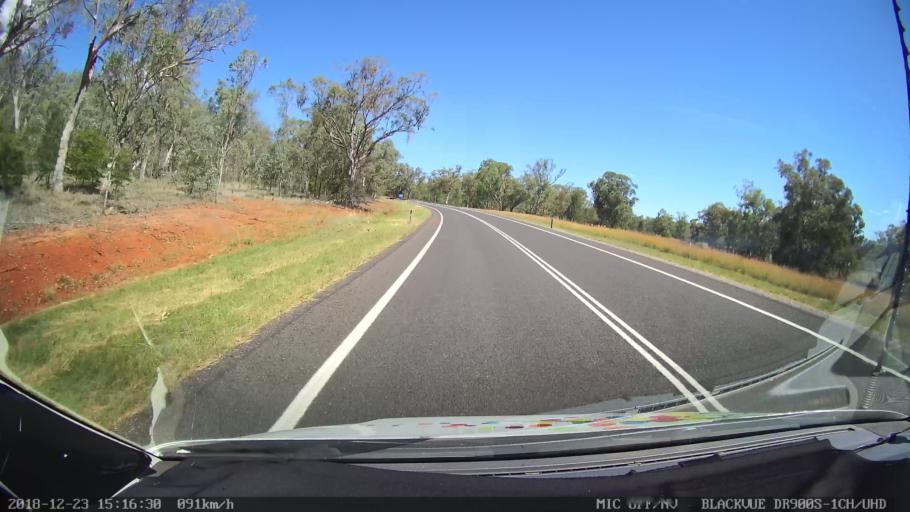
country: AU
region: New South Wales
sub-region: Tamworth Municipality
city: Manilla
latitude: -30.7997
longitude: 150.7486
